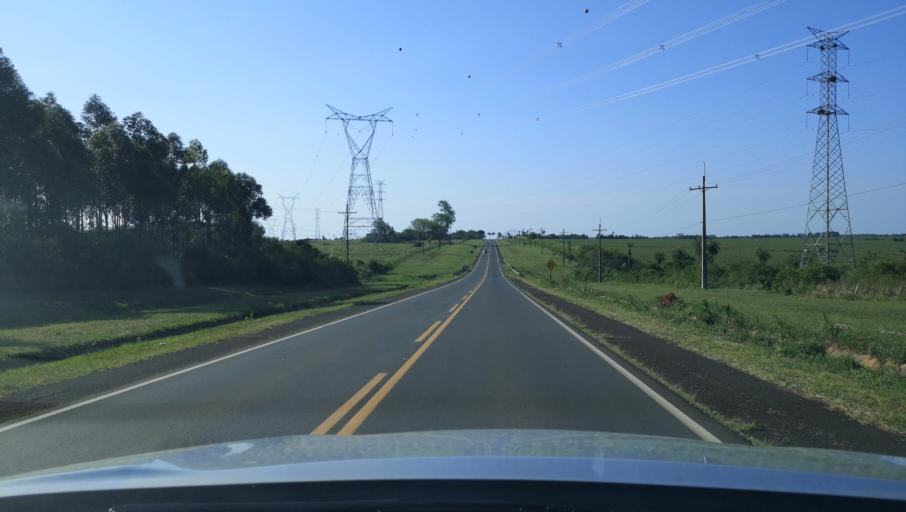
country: PY
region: Misiones
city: Santa Maria
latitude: -26.7906
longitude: -57.0247
